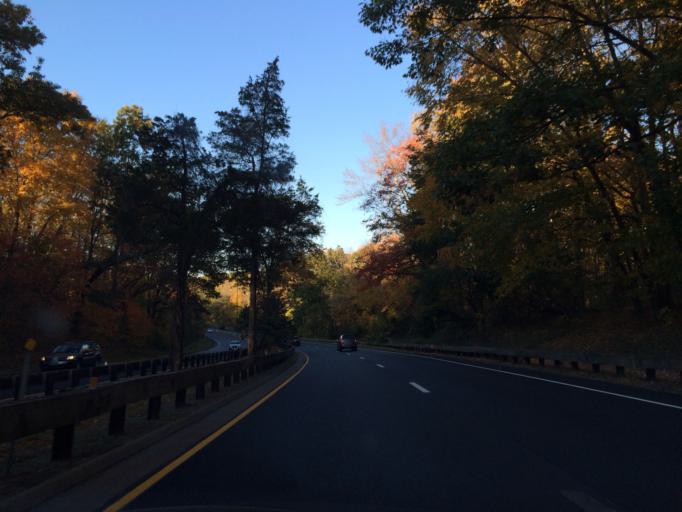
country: US
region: Connecticut
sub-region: Fairfield County
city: Glenville
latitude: 41.0658
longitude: -73.6709
